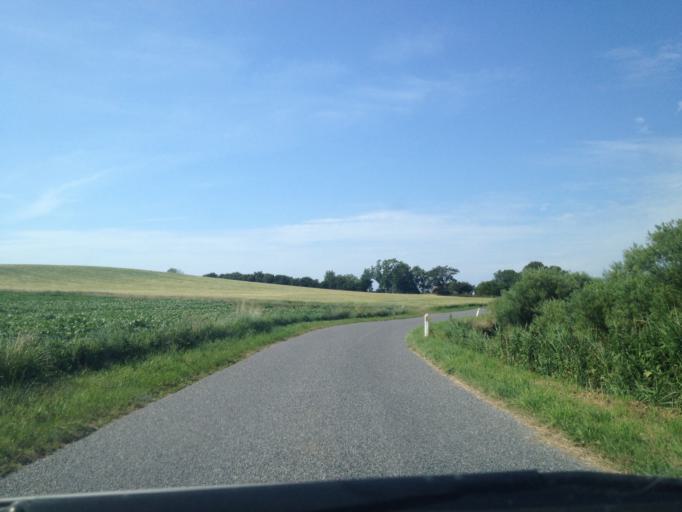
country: DK
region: Central Jutland
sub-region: Samso Kommune
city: Tranebjerg
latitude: 55.8355
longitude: 10.5550
